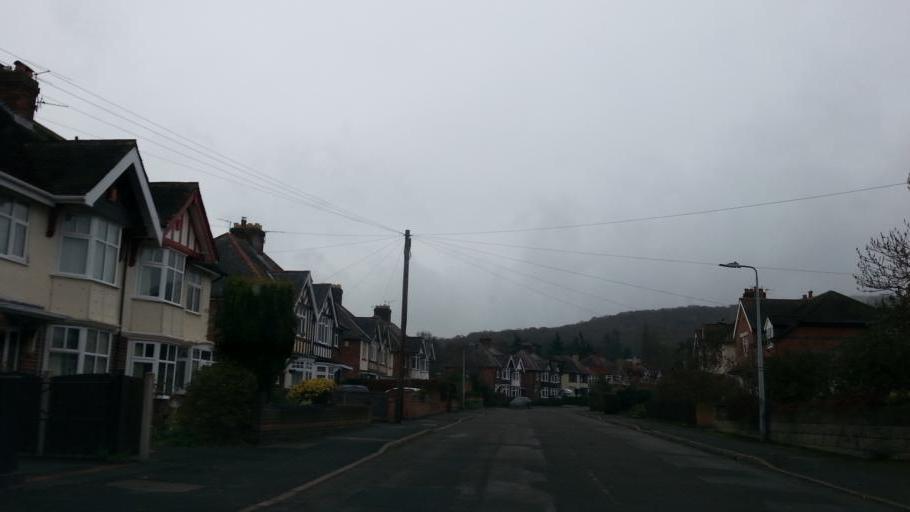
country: GB
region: England
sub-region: Telford and Wrekin
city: Wellington
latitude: 52.6950
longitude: -2.5284
